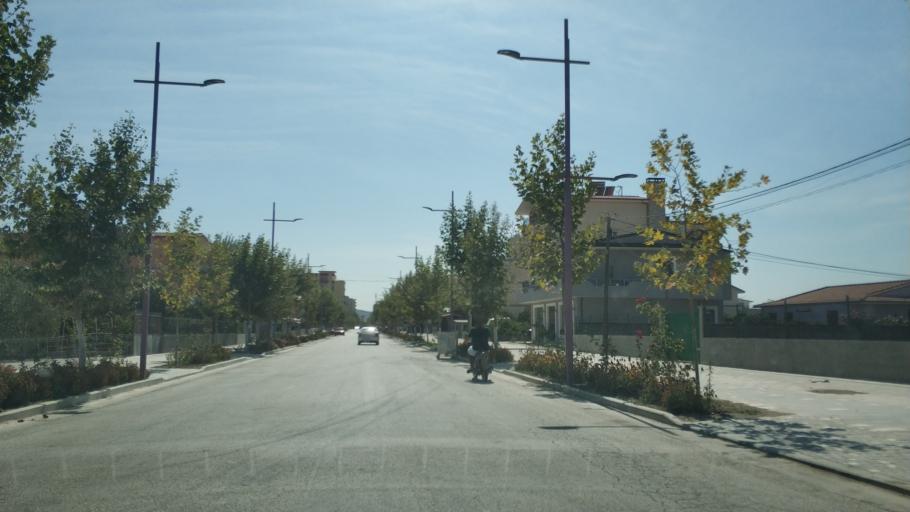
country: AL
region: Fier
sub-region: Rrethi i Lushnjes
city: Divjake
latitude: 41.0017
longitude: 19.5305
